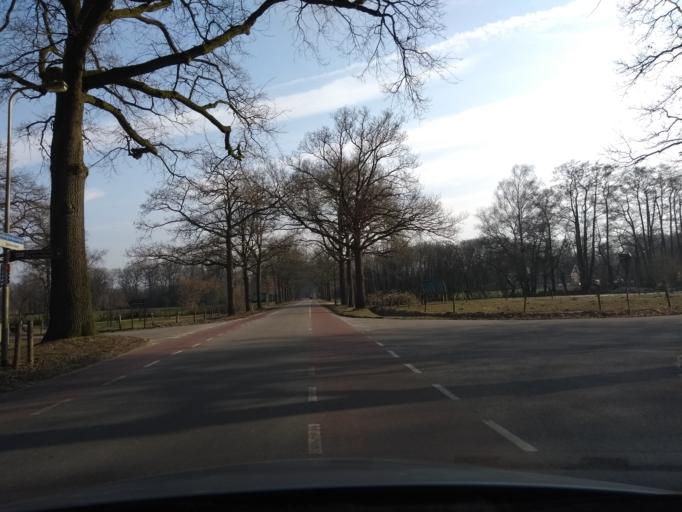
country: NL
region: Overijssel
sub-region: Gemeente Hengelo
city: Hengelo
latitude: 52.2312
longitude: 6.8125
